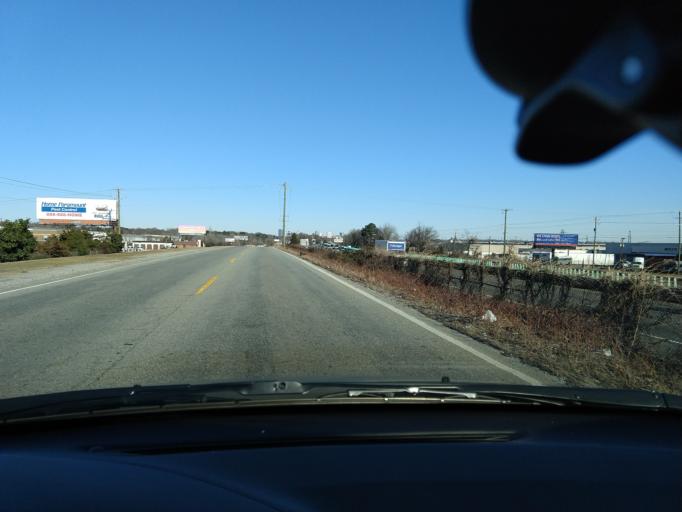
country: US
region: Virginia
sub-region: Chesterfield County
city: Bensley
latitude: 37.4864
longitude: -77.4324
